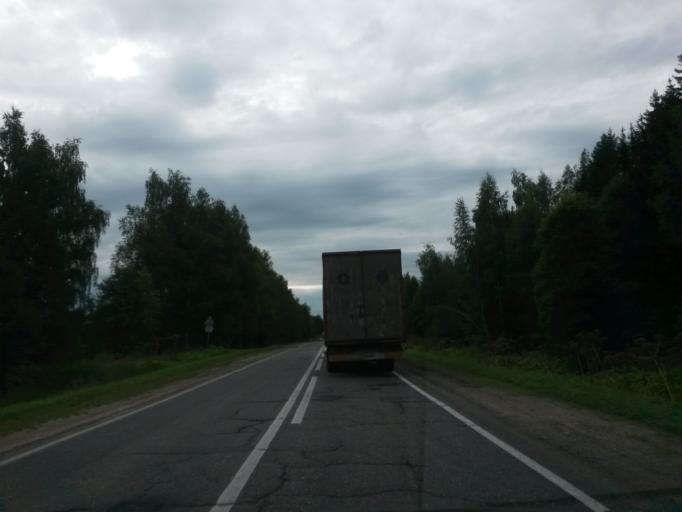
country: RU
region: Jaroslavl
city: Gavrilov-Yam
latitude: 57.3648
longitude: 39.7416
